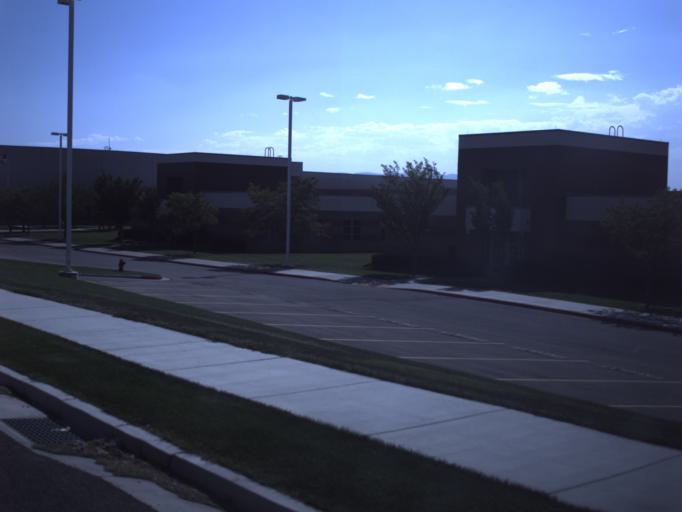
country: US
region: Utah
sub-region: Utah County
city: Cedar Hills
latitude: 40.4188
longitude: -111.7736
